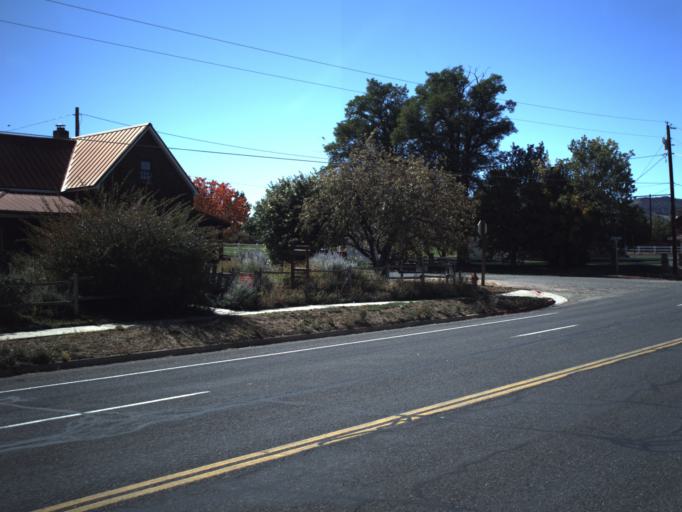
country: US
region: Utah
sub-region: Wayne County
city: Loa
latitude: 37.7703
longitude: -111.5978
